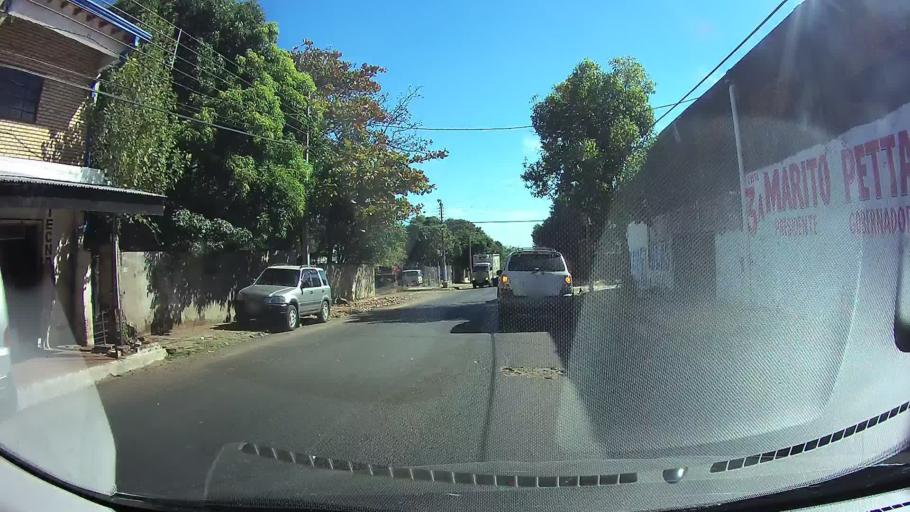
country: PY
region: Central
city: Lambare
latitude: -25.3456
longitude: -57.5842
